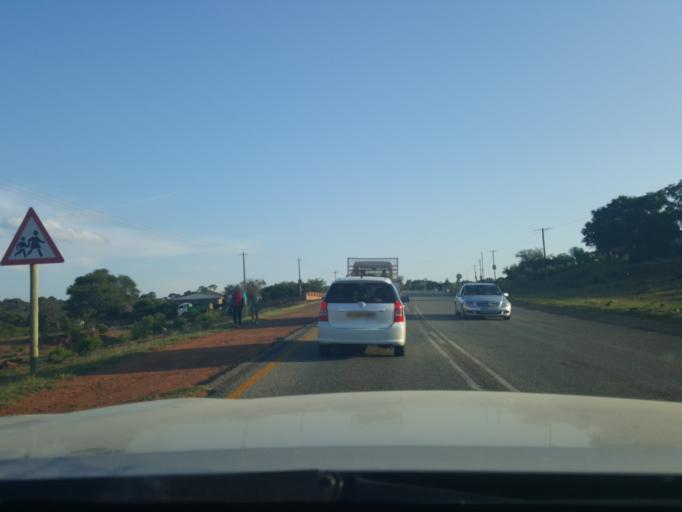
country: ZA
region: North-West
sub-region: Ngaka Modiri Molema District Municipality
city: Zeerust
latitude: -25.3254
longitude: 26.1218
